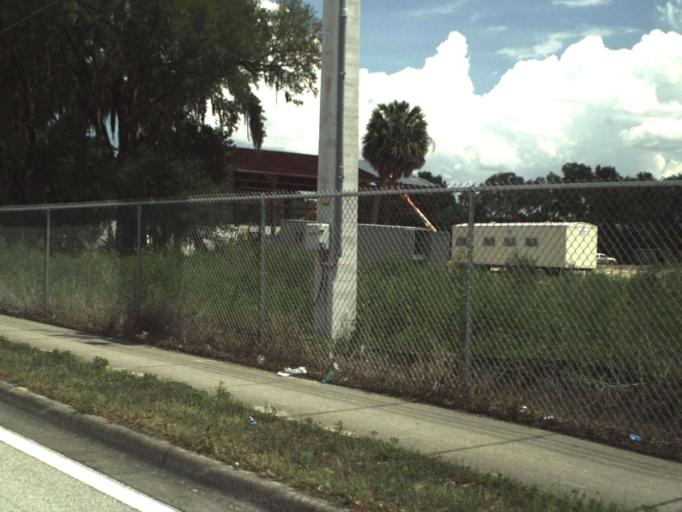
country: US
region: Florida
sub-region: Lake County
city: Leesburg
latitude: 28.8030
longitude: -81.9110
